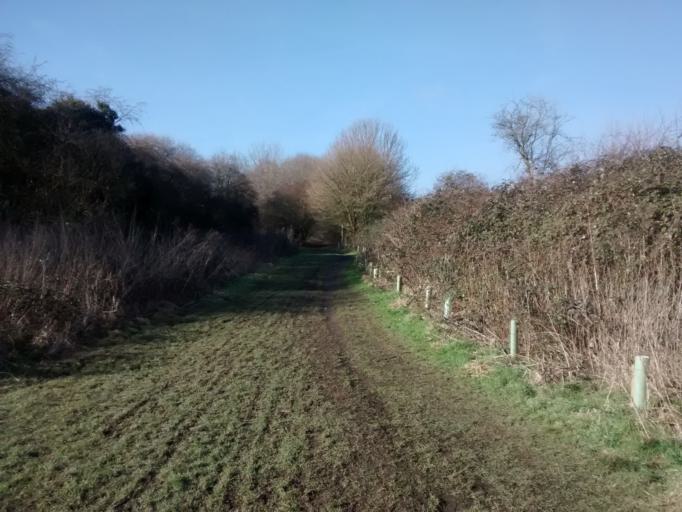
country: GB
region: England
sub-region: South Gloucestershire
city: Almondsbury
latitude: 51.5387
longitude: -2.5785
